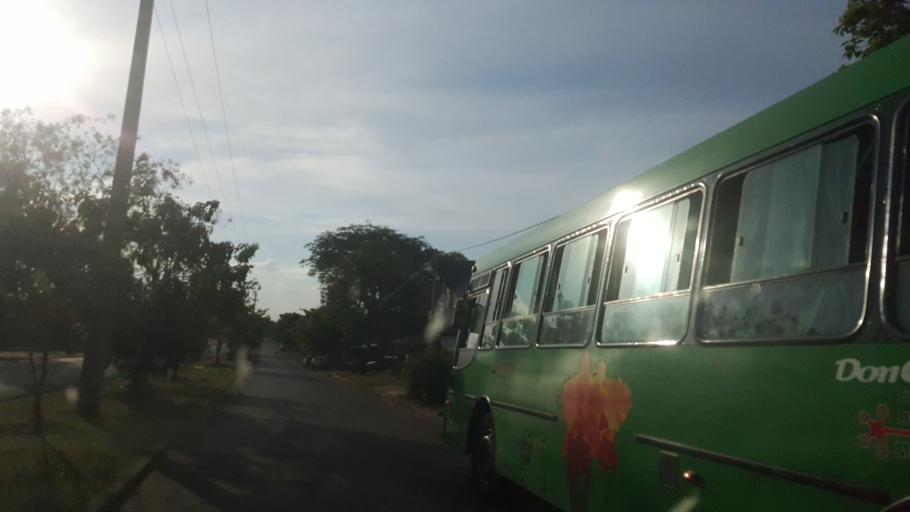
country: AR
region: Misiones
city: Garupa
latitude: -27.4344
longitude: -55.8703
